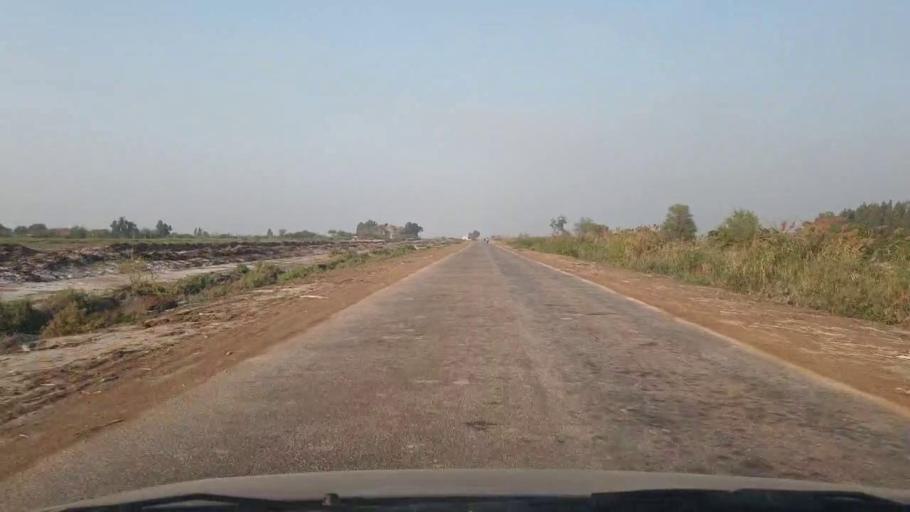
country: PK
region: Sindh
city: Mirwah Gorchani
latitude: 25.3429
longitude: 69.1702
